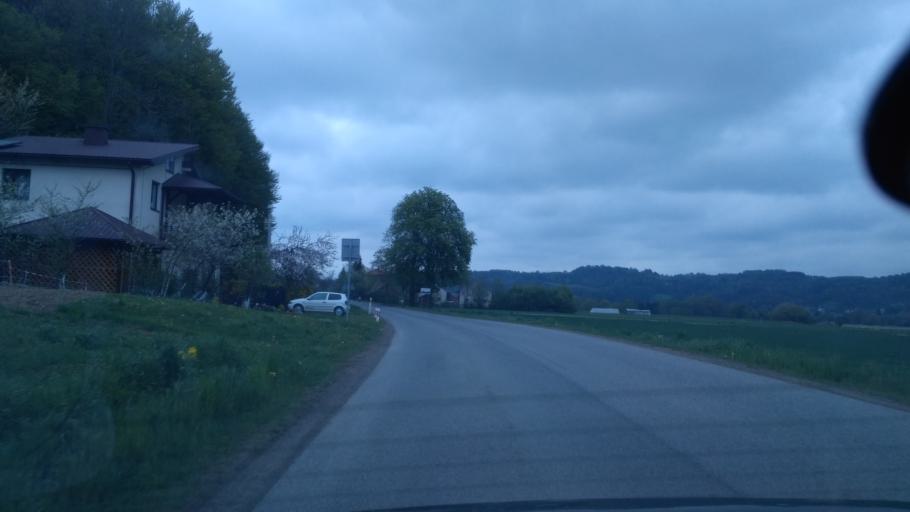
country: PL
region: Subcarpathian Voivodeship
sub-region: Powiat brzozowski
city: Nozdrzec
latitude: 49.7500
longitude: 22.2207
